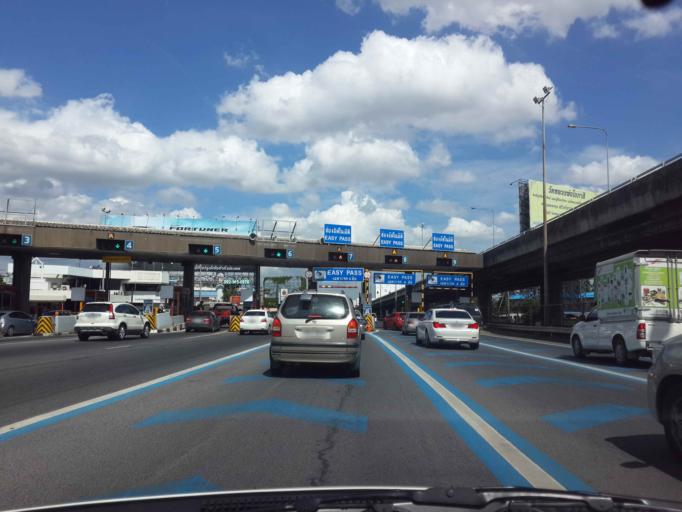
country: TH
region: Bangkok
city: Chom Thong
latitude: 13.6758
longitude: 100.4807
